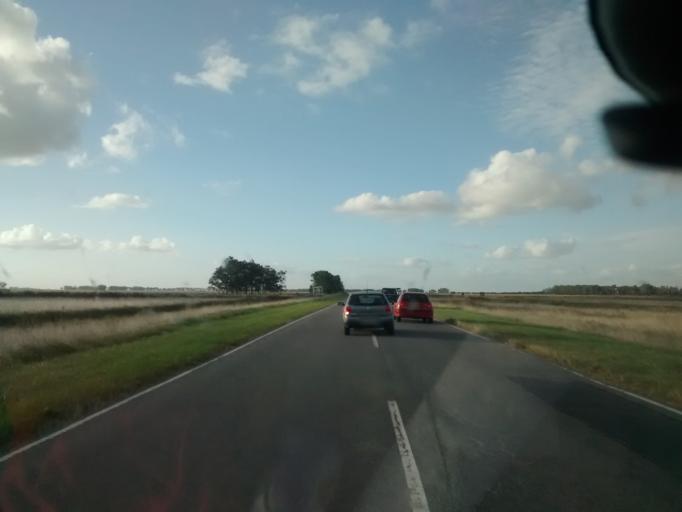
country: AR
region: Buenos Aires
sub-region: Partido de General Belgrano
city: General Belgrano
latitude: -36.1905
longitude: -58.5930
